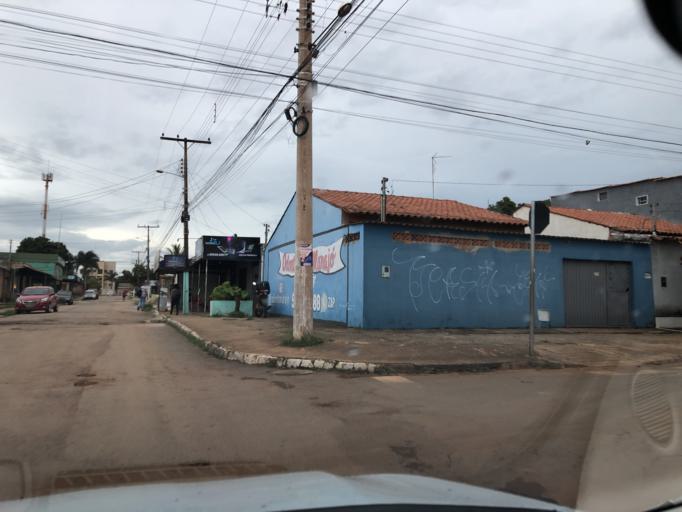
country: BR
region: Goias
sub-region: Luziania
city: Luziania
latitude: -16.1109
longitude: -47.9727
